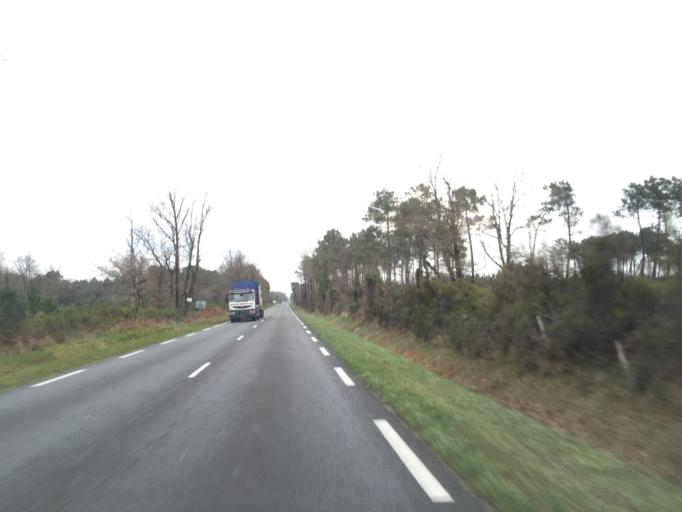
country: FR
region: Aquitaine
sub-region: Departement de la Gironde
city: Saint-Sauveur
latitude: 45.1787
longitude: -0.8419
